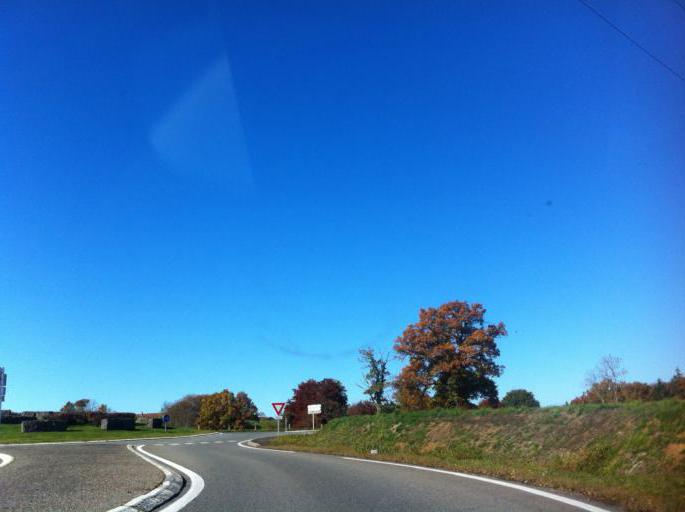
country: FR
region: Auvergne
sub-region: Departement du Puy-de-Dome
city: Gelles
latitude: 45.8679
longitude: 2.6718
